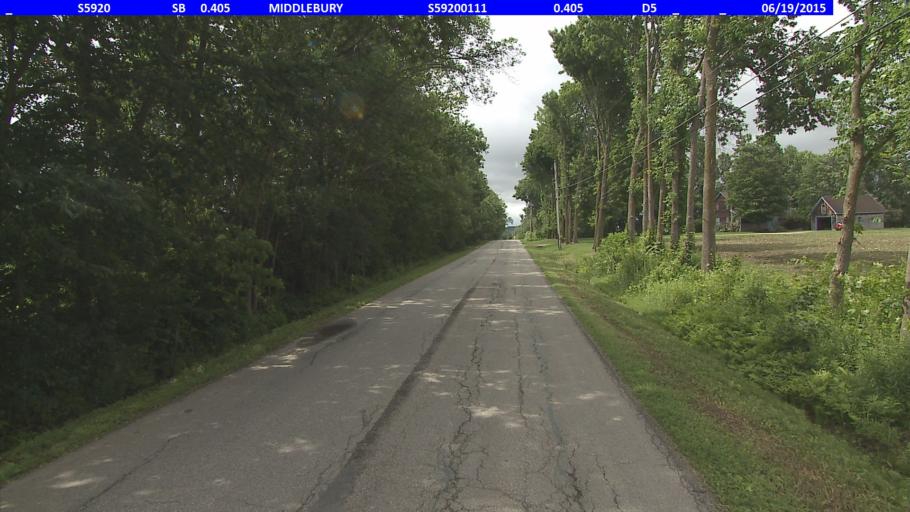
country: US
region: Vermont
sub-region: Addison County
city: Middlebury (village)
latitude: 43.9940
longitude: -73.1345
